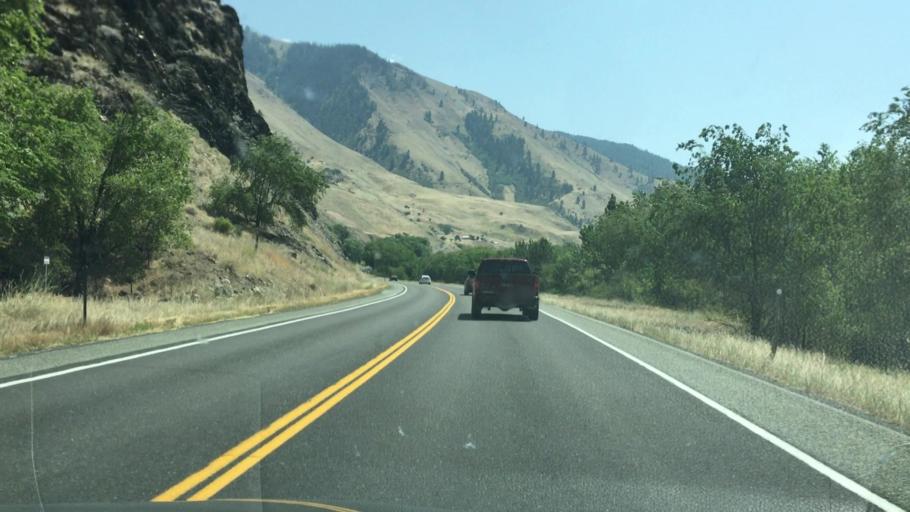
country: US
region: Idaho
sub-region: Valley County
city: McCall
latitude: 45.3476
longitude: -116.3549
